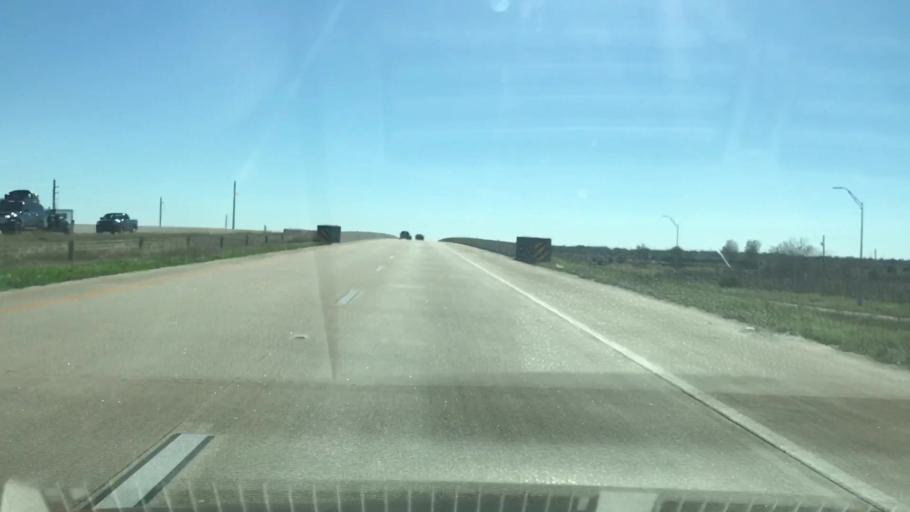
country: US
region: Texas
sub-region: Harris County
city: Cypress
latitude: 29.9803
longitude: -95.7697
